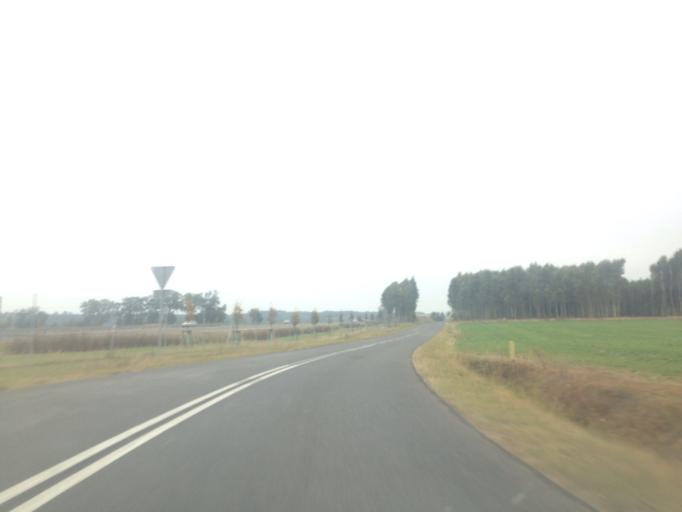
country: PL
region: Greater Poland Voivodeship
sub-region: Powiat gnieznienski
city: Lubowo
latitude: 52.4728
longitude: 17.4081
